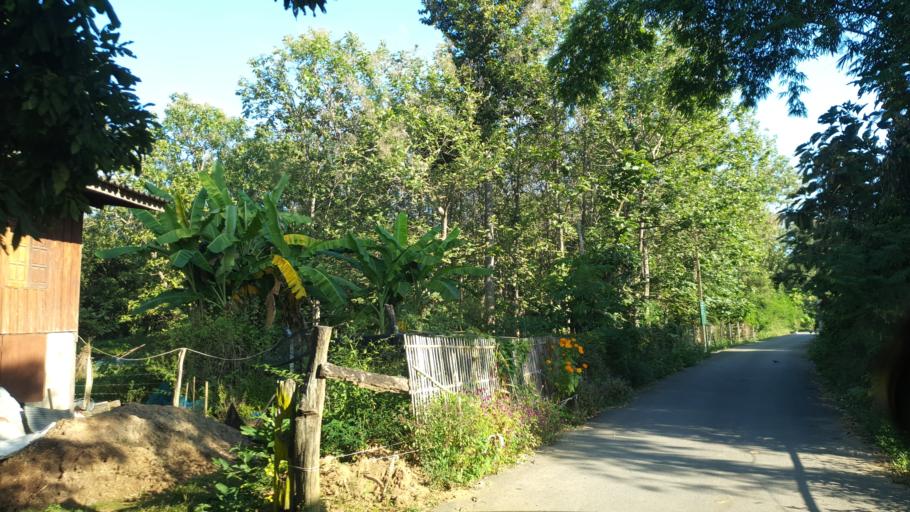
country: TH
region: Chiang Mai
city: Mae On
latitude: 18.7376
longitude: 99.2159
